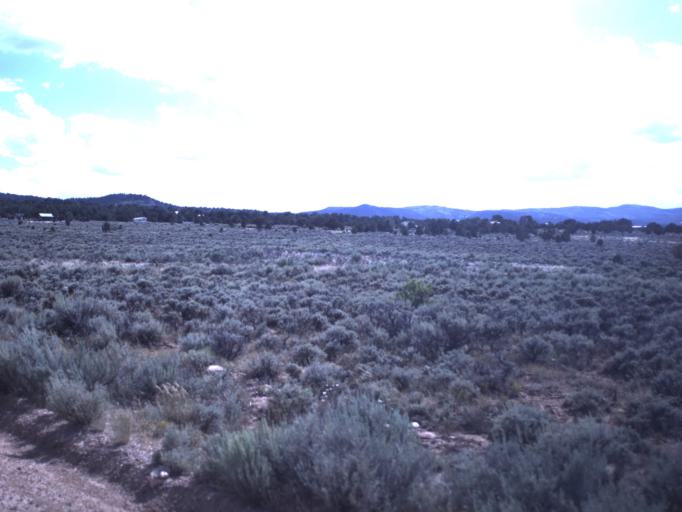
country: US
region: Utah
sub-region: Duchesne County
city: Duchesne
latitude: 40.2041
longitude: -110.7316
